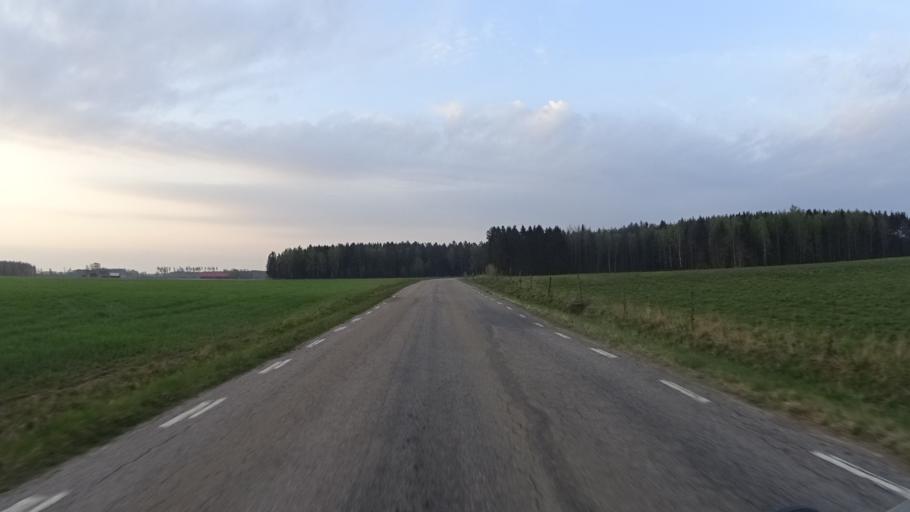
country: SE
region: Vaestra Goetaland
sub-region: Gotene Kommun
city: Kallby
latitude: 58.4611
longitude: 13.3357
